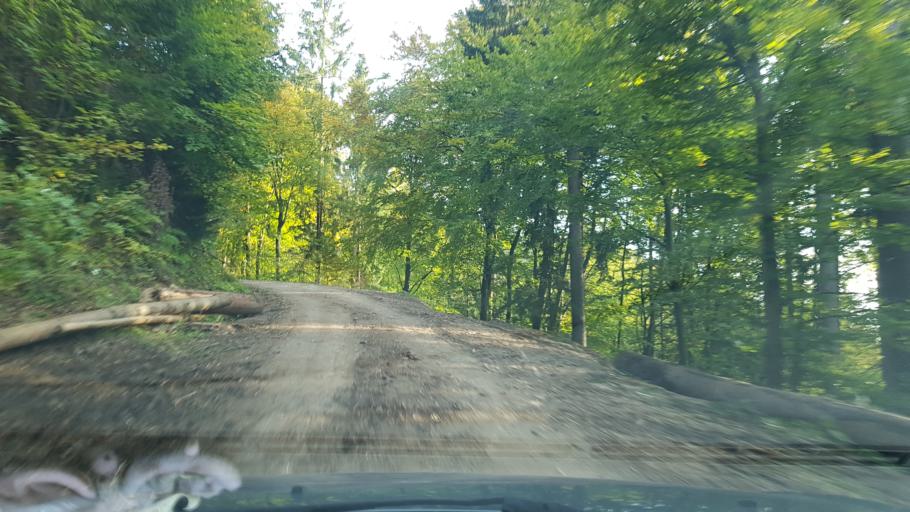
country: SI
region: Slovenj Gradec
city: Legen
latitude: 46.5183
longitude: 15.1320
